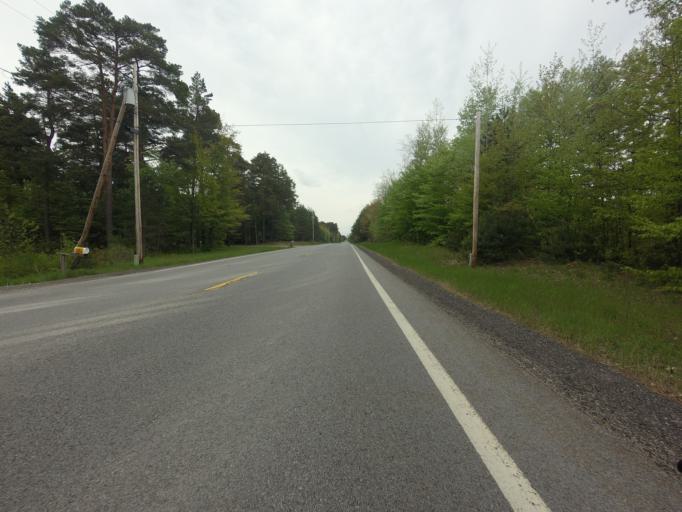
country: US
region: New York
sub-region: St. Lawrence County
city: Hannawa Falls
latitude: 44.6596
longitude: -74.7518
